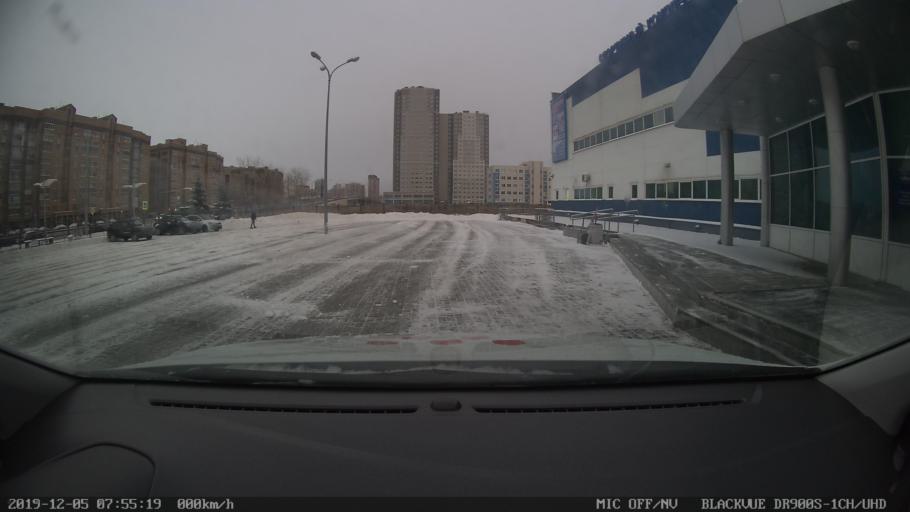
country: RU
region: Tatarstan
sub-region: Gorod Kazan'
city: Kazan
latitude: 55.8199
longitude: 49.1397
